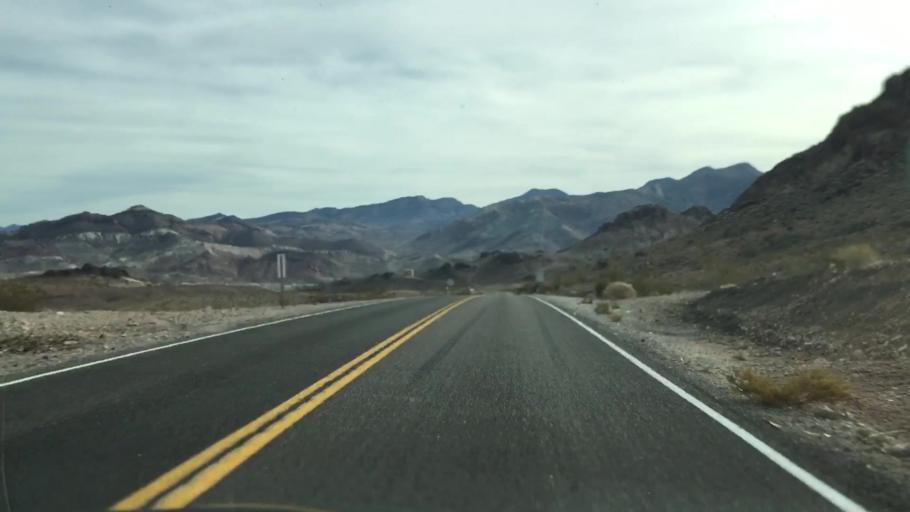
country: US
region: Nevada
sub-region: Nye County
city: Beatty
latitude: 36.9033
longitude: -116.7835
